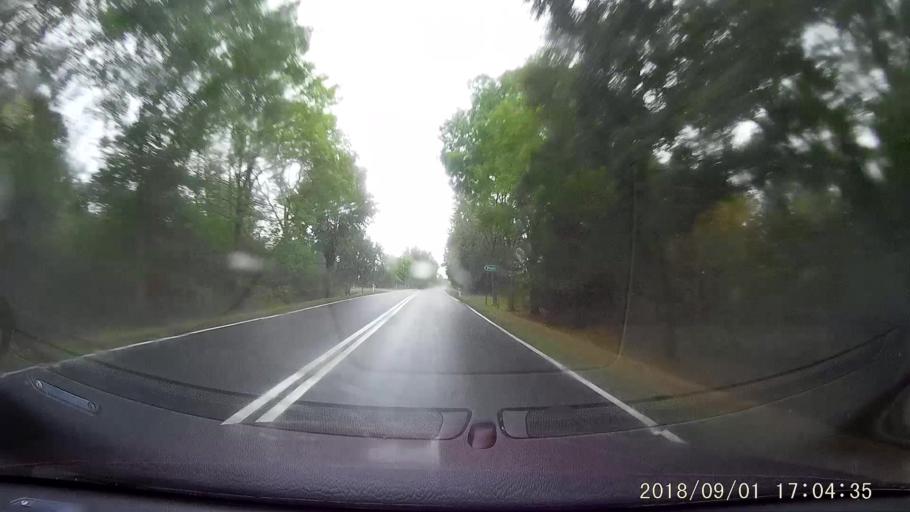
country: PL
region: Lubusz
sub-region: Powiat zielonogorski
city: Swidnica
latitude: 51.8638
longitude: 15.3603
